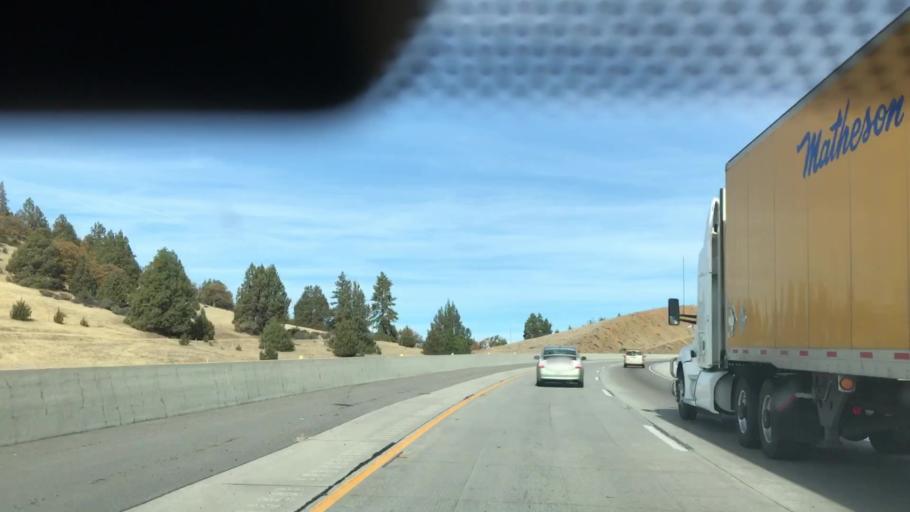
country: US
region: California
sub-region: Siskiyou County
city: Yreka
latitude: 41.7906
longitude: -122.5887
